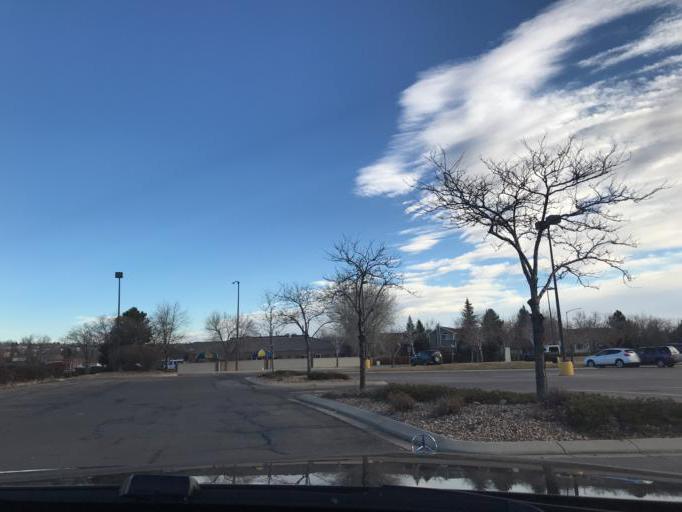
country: US
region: Colorado
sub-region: Boulder County
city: Superior
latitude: 39.9635
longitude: -105.1614
